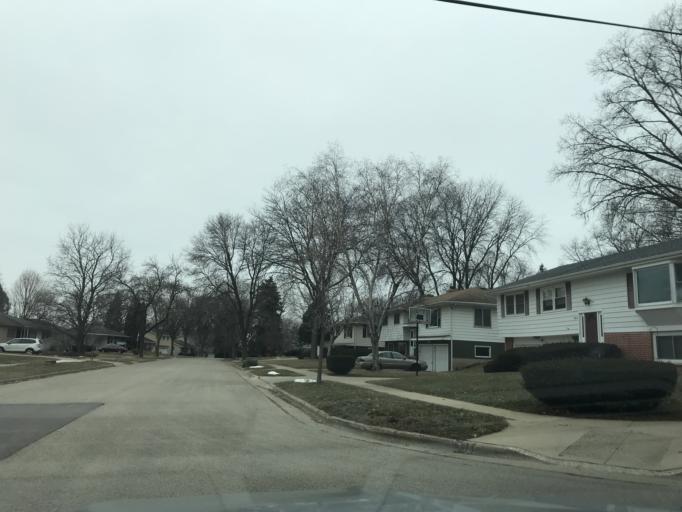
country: US
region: Wisconsin
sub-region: Dane County
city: Monona
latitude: 43.0894
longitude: -89.2992
